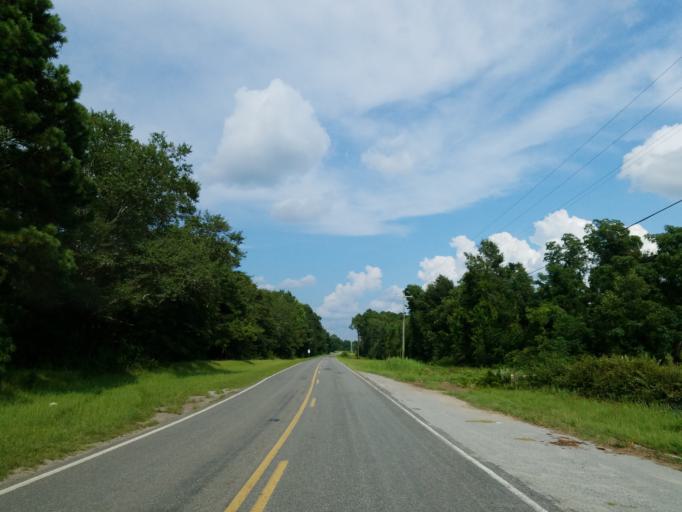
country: US
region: Georgia
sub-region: Dooly County
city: Unadilla
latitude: 32.1914
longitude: -83.7456
